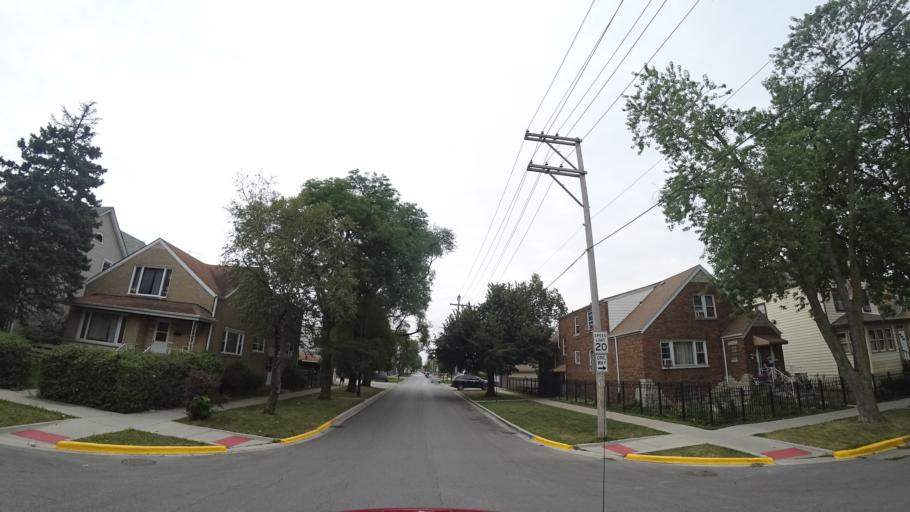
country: US
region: Illinois
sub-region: Cook County
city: Cicero
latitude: 41.8485
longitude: -87.7515
